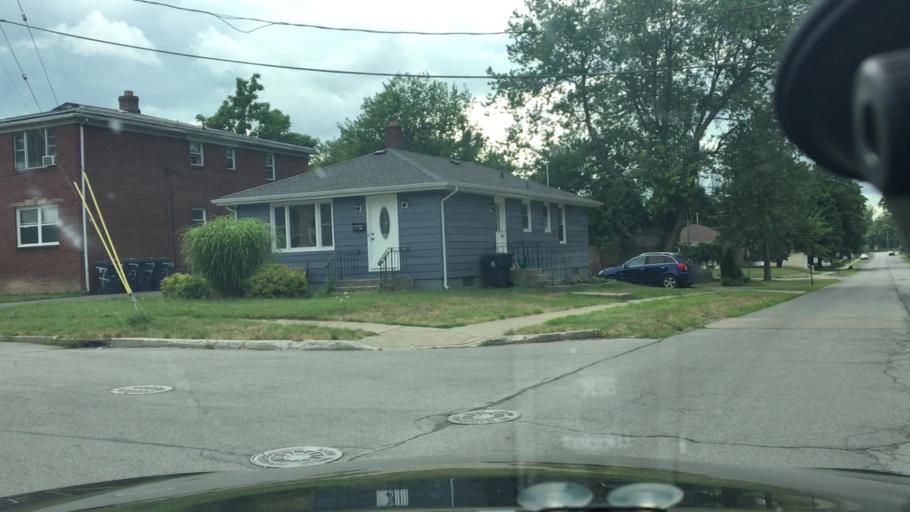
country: US
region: New York
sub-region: Erie County
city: Lackawanna
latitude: 42.8320
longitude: -78.8186
